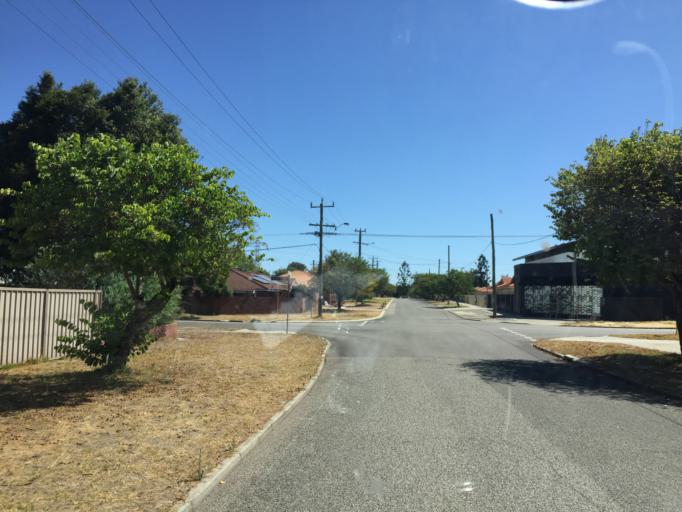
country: AU
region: Western Australia
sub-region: Victoria Park
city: Victoria Park
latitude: -31.9808
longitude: 115.9146
